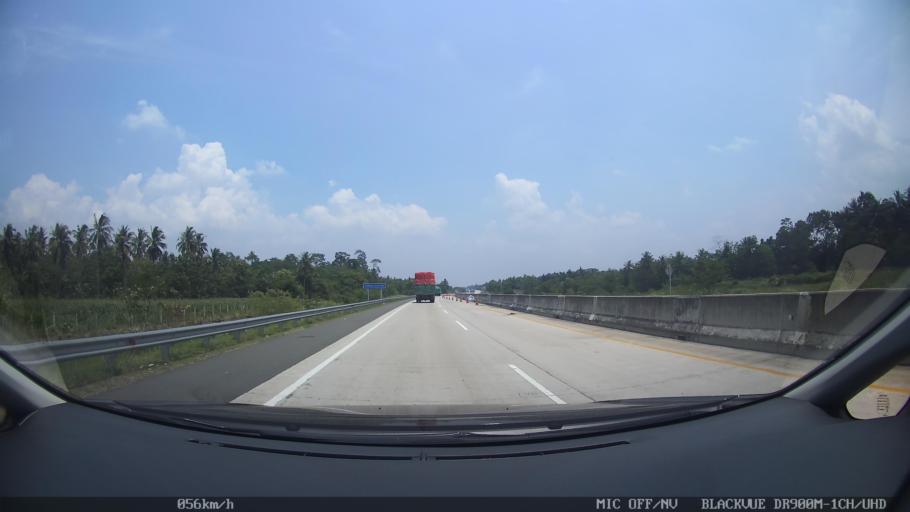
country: ID
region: Lampung
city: Natar
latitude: -5.3160
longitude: 105.2596
